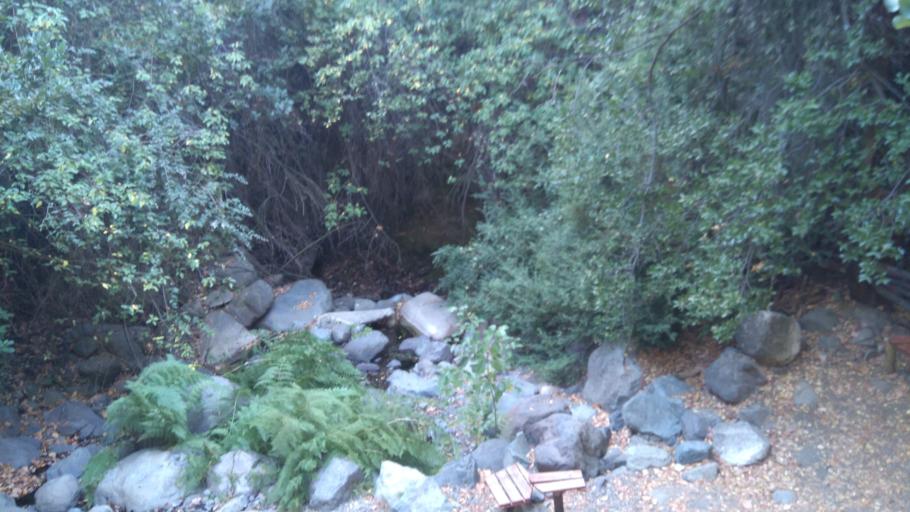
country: CL
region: Santiago Metropolitan
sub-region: Provincia de Cordillera
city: Puente Alto
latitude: -33.7166
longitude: -70.4621
